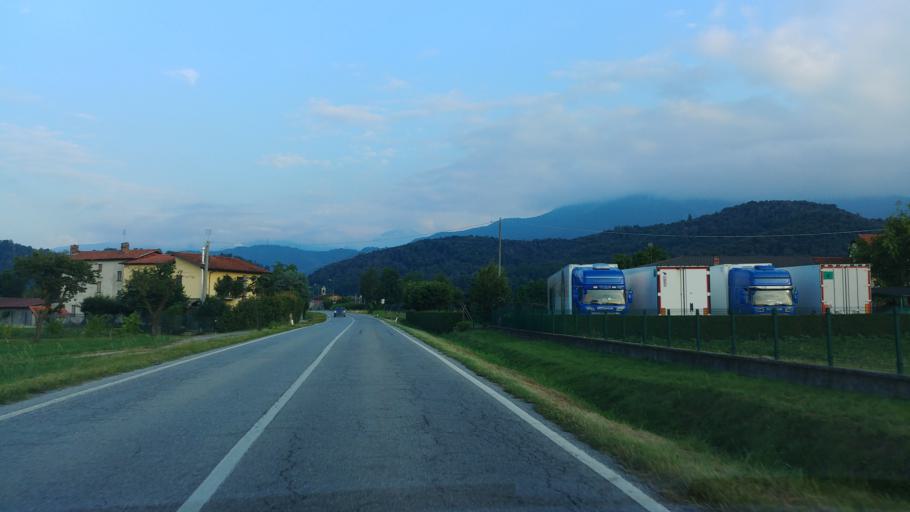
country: IT
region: Piedmont
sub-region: Provincia di Cuneo
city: Peveragno
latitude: 44.3414
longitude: 7.5991
